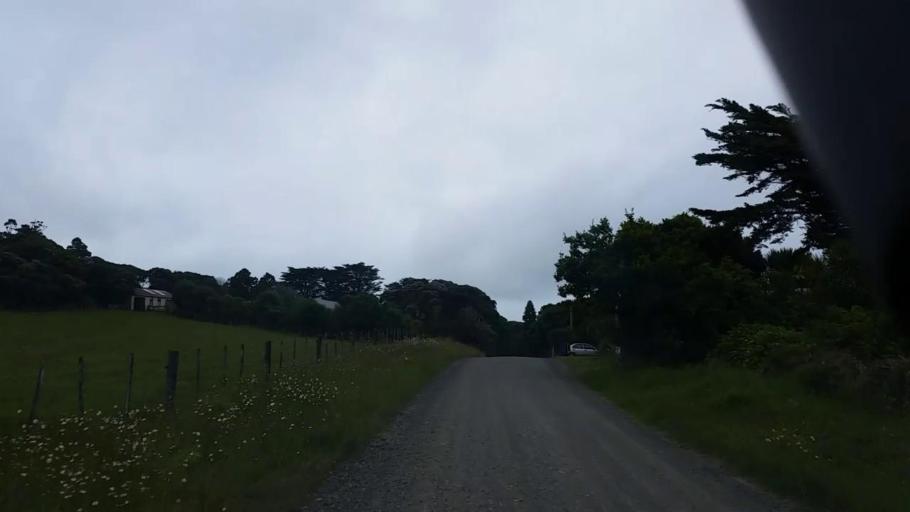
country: NZ
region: Auckland
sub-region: Auckland
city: Muriwai Beach
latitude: -36.9284
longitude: 174.4768
